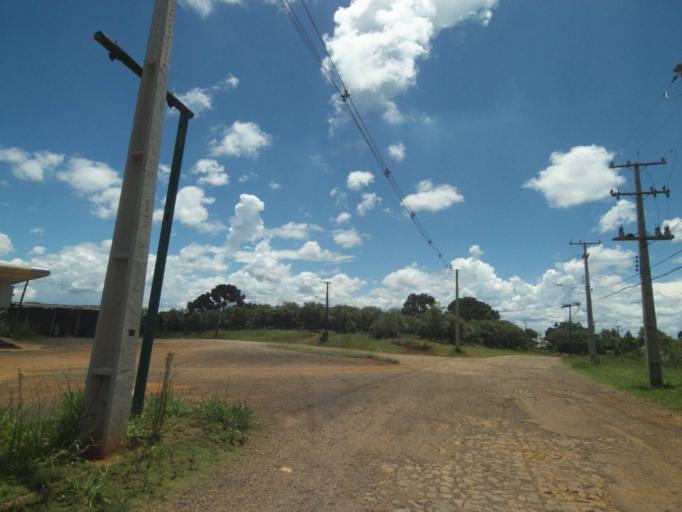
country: BR
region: Parana
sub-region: Pinhao
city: Pinhao
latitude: -25.7914
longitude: -52.0817
